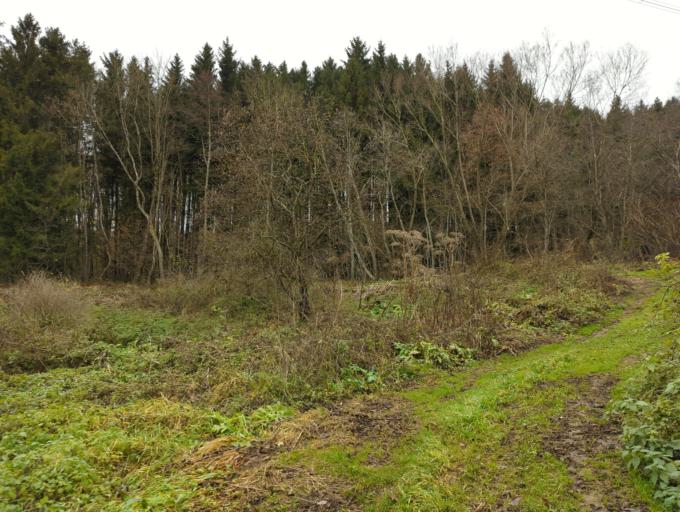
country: DE
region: Bavaria
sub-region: Swabia
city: Guenzburg
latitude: 48.4391
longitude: 10.3097
